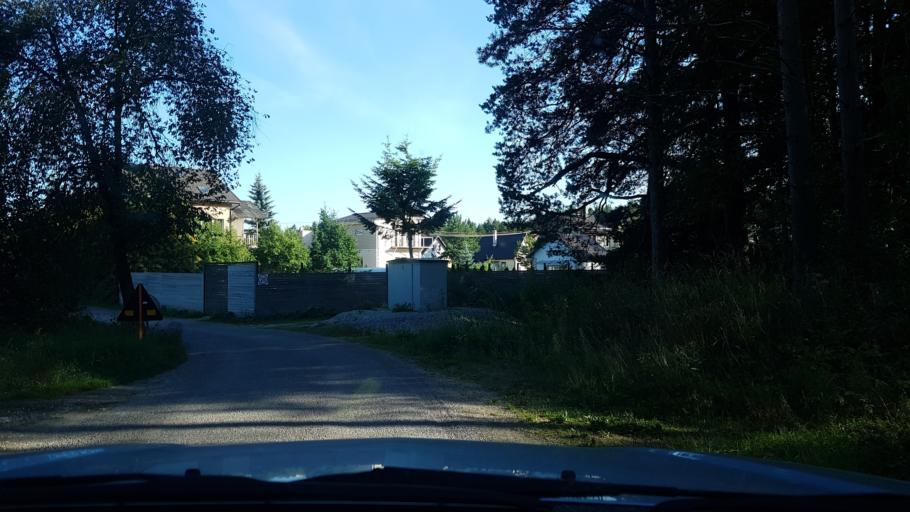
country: EE
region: Ida-Virumaa
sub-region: Narva-Joesuu linn
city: Narva-Joesuu
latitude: 59.4463
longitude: 28.0719
